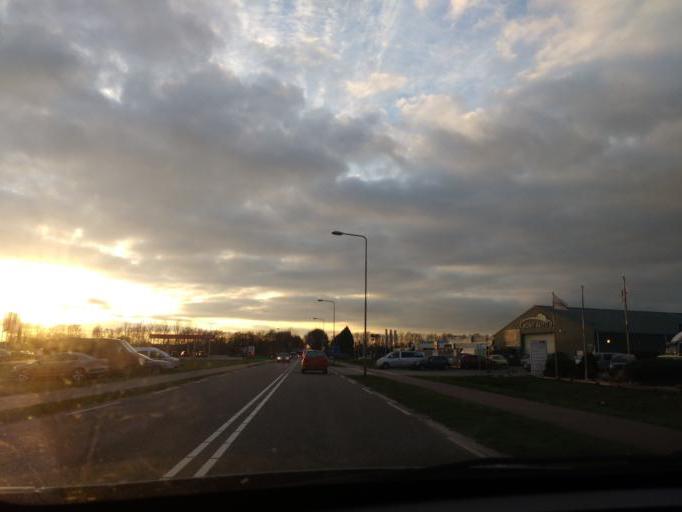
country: NL
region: Limburg
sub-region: Gemeente Venray
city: Venray
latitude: 51.5250
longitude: 6.0061
